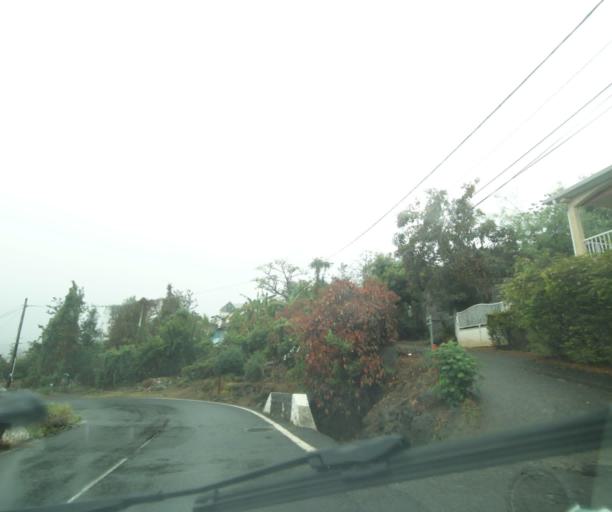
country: RE
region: Reunion
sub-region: Reunion
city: Saint-Paul
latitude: -21.0252
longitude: 55.2872
